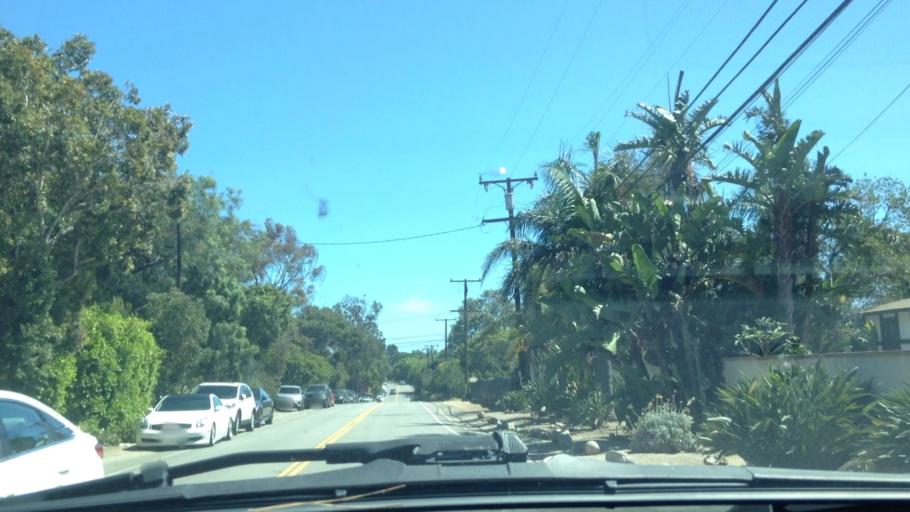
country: US
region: California
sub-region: Los Angeles County
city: Malibu
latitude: 34.0116
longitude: -118.8011
